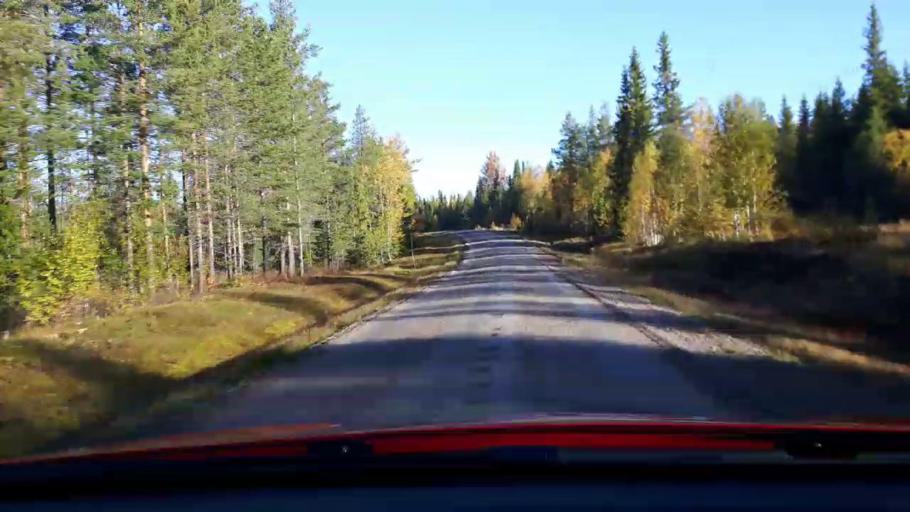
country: SE
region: Jaemtland
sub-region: Stroemsunds Kommun
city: Stroemsund
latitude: 64.3928
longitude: 15.1493
